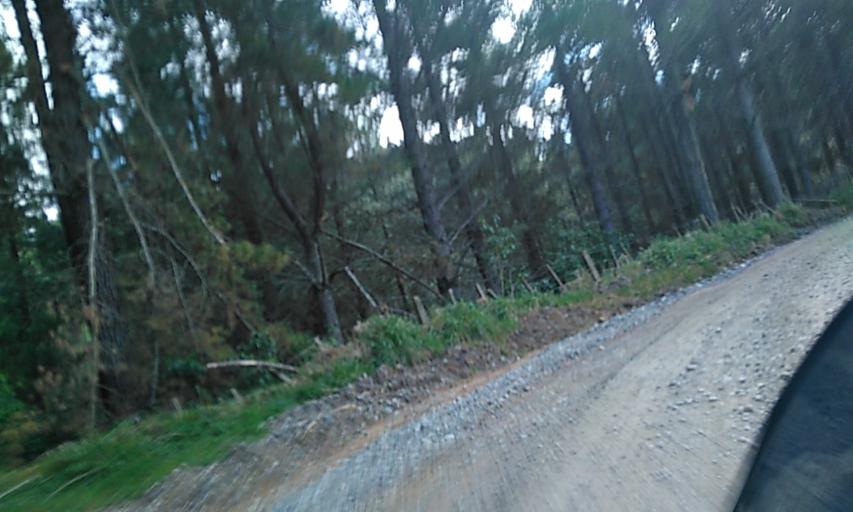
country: NZ
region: Gisborne
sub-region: Gisborne District
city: Gisborne
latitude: -38.3252
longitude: 178.0729
